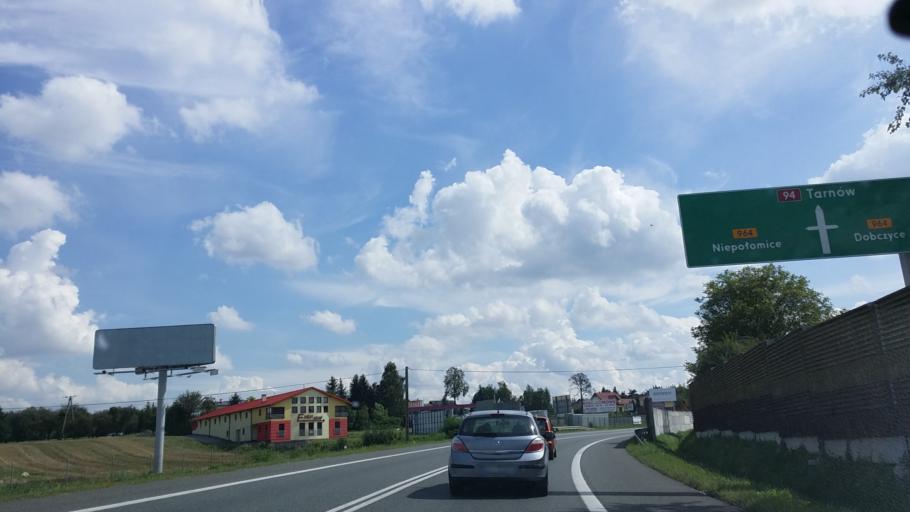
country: PL
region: Lesser Poland Voivodeship
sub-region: Powiat wielicki
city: Wieliczka
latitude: 49.9925
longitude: 20.0800
